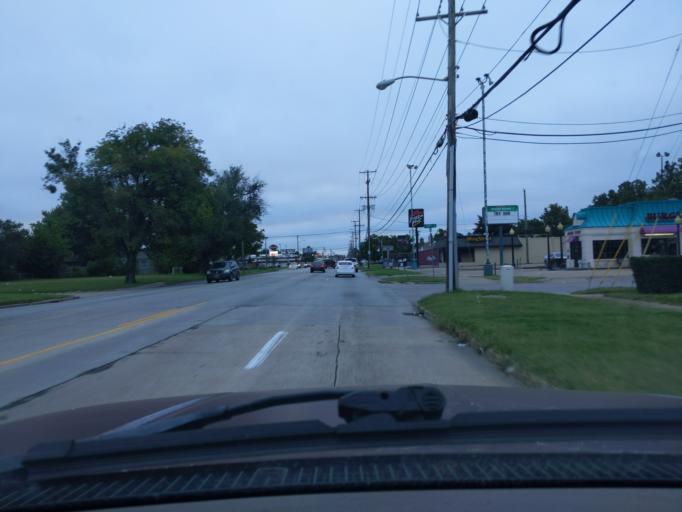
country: US
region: Oklahoma
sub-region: Tulsa County
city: Tulsa
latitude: 36.0919
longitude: -95.9757
